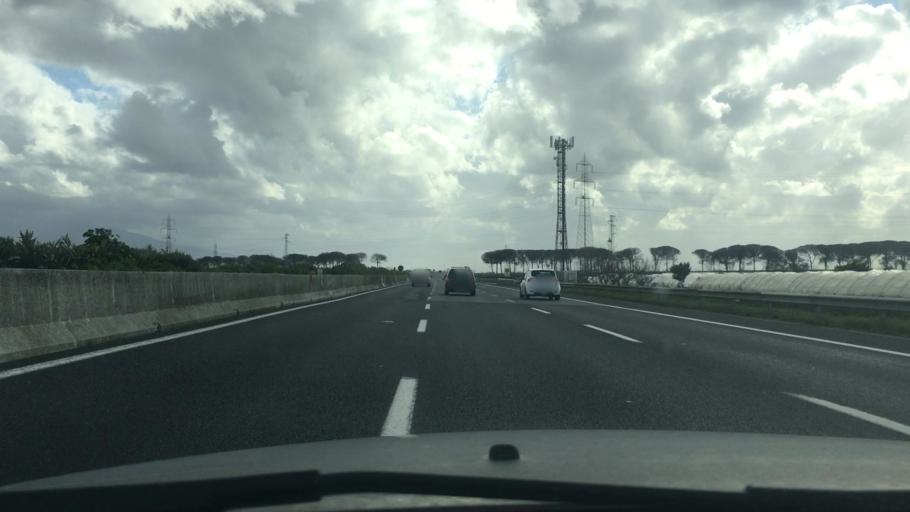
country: IT
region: Campania
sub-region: Provincia di Napoli
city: Pascarola
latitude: 40.9921
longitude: 14.3246
